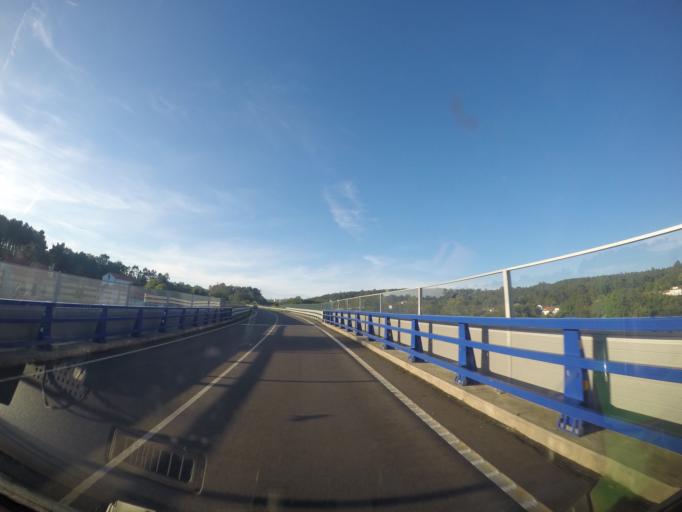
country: ES
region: Galicia
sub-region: Provincia da Coruna
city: Noia
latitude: 42.8002
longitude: -8.8889
